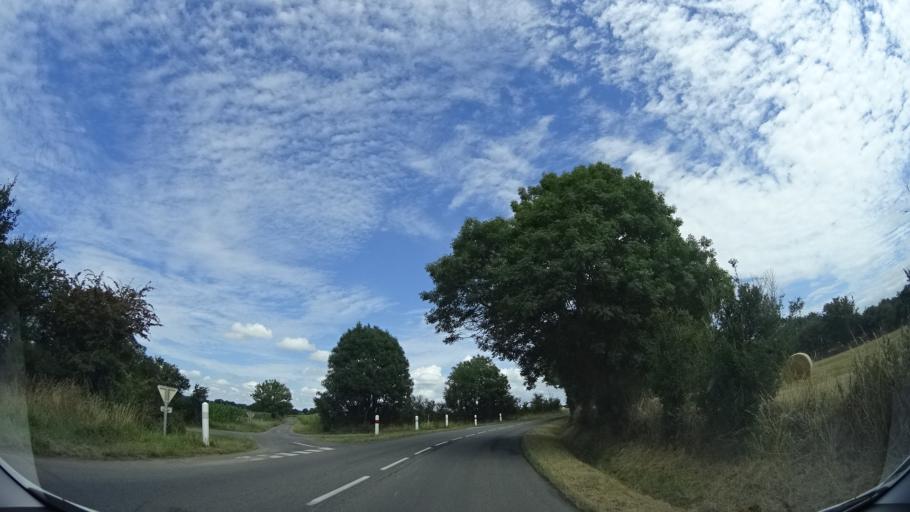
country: FR
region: Lower Normandy
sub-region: Departement de la Manche
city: Marcey-les-Greves
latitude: 48.6891
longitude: -1.4537
